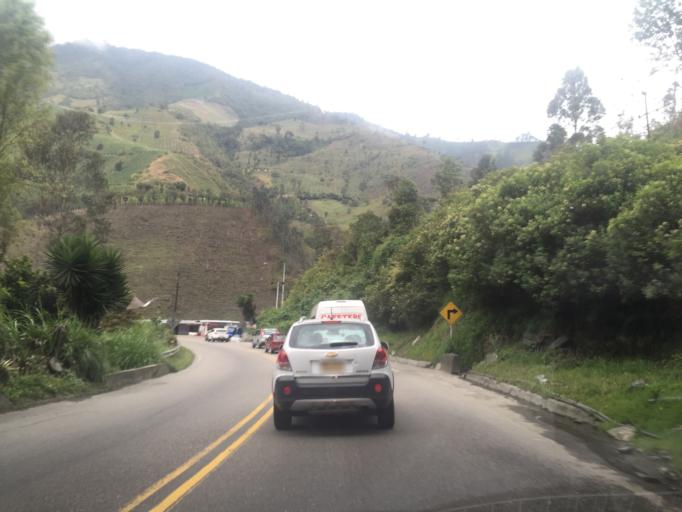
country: CO
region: Tolima
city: Cajamarca
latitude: 4.4341
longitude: -75.4644
